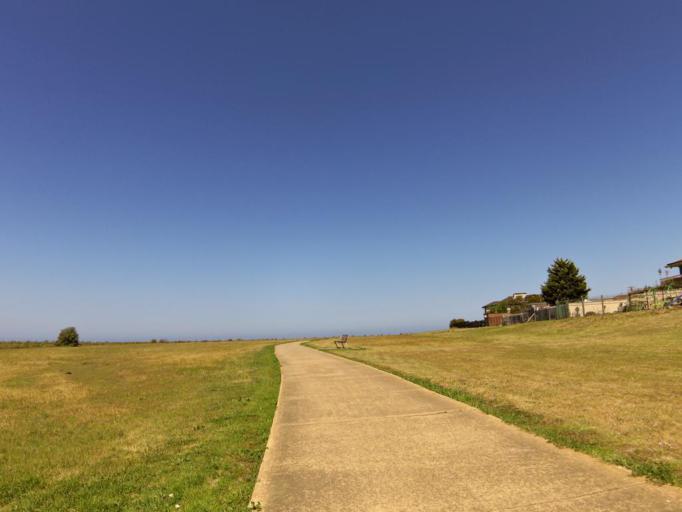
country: AU
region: Victoria
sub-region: Hobsons Bay
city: Altona Meadows
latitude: -37.8898
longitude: 144.7872
